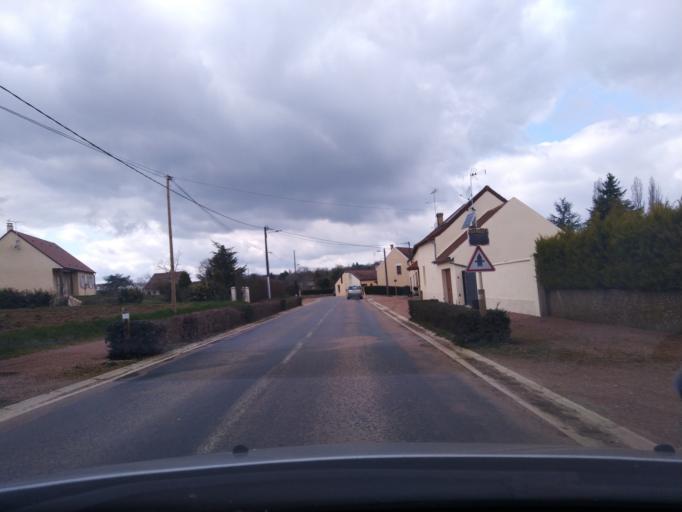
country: FR
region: Bourgogne
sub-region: Departement de l'Yonne
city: Avallon
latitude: 47.5186
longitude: 3.9502
